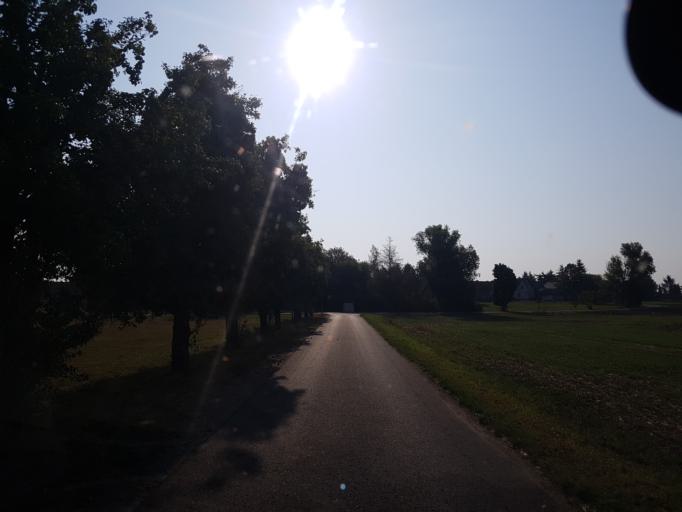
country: DE
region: Brandenburg
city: Finsterwalde
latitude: 51.6866
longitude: 13.7172
